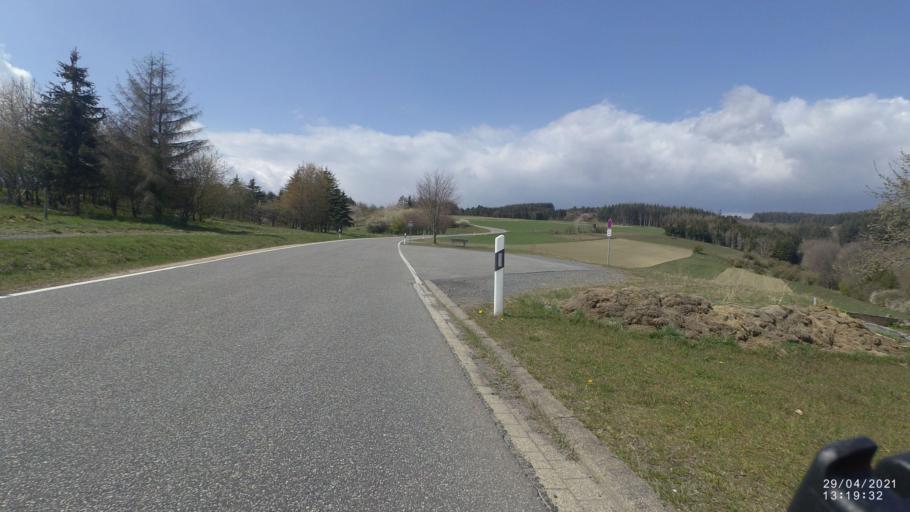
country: DE
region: Rheinland-Pfalz
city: Arft
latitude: 50.3820
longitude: 7.0795
